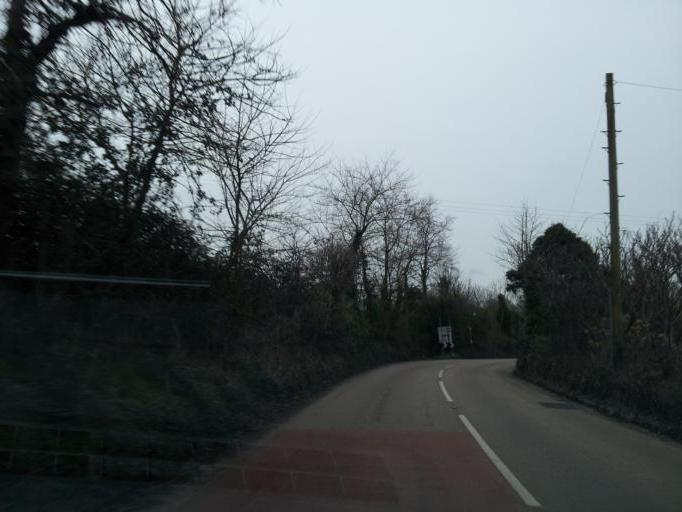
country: GB
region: England
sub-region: Cornwall
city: Redruth
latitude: 50.2400
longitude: -5.2386
